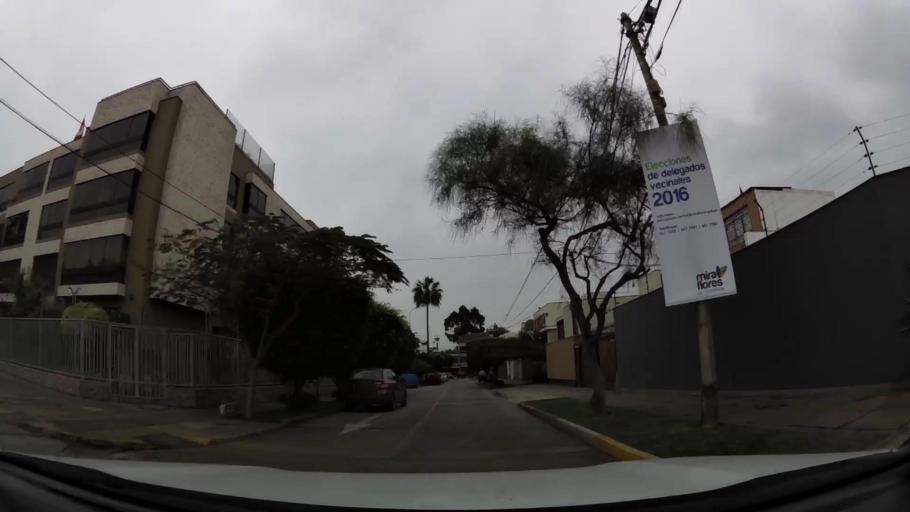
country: PE
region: Lima
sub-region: Lima
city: Surco
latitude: -12.1286
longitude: -77.0148
